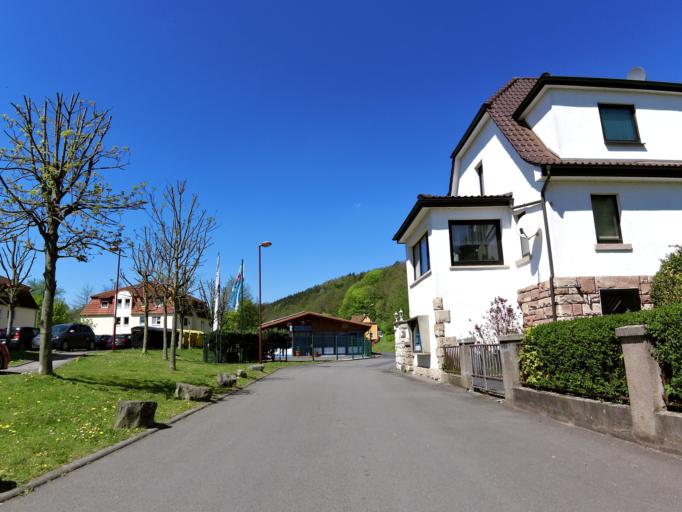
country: DE
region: Thuringia
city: Bad Salzungen
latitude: 50.8175
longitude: 10.2543
